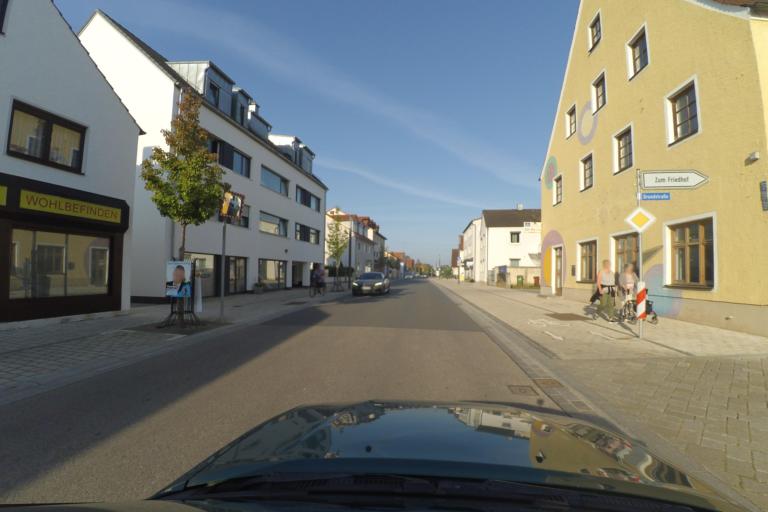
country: DE
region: Bavaria
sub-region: Upper Bavaria
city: Manching
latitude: 48.7171
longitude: 11.4904
